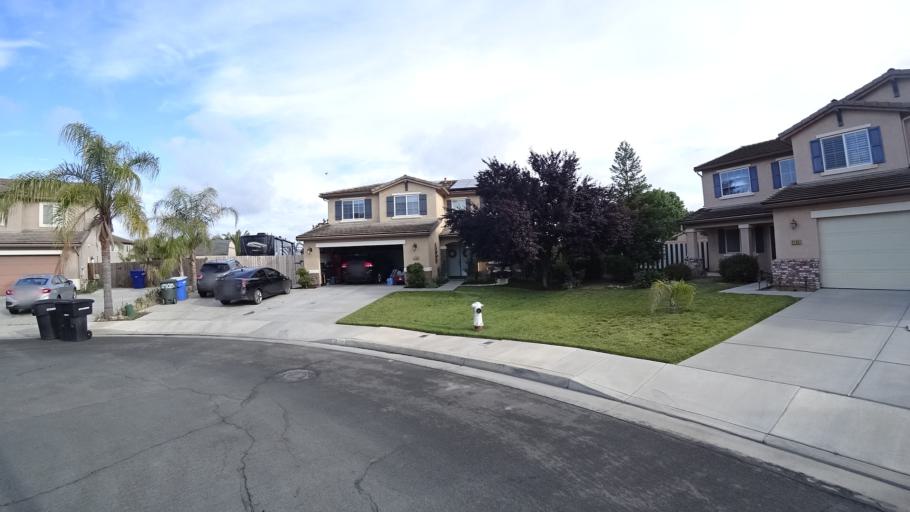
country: US
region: California
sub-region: Kings County
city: Lucerne
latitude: 36.3495
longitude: -119.6783
